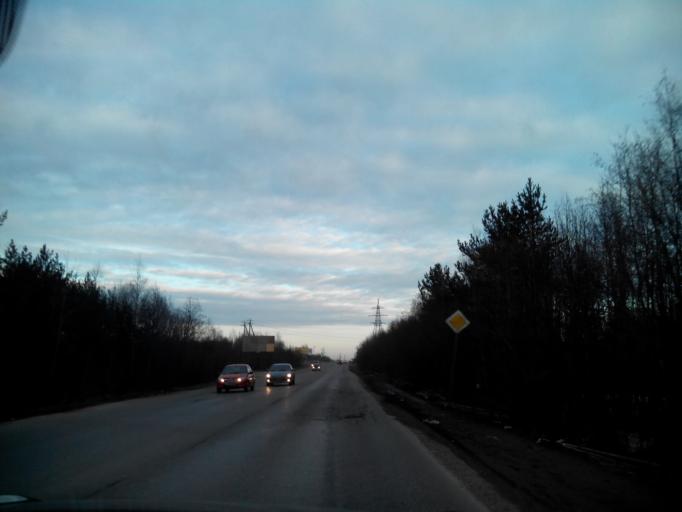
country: RU
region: Arkhangelskaya
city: Arkhangel'sk
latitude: 64.5216
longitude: 40.6716
